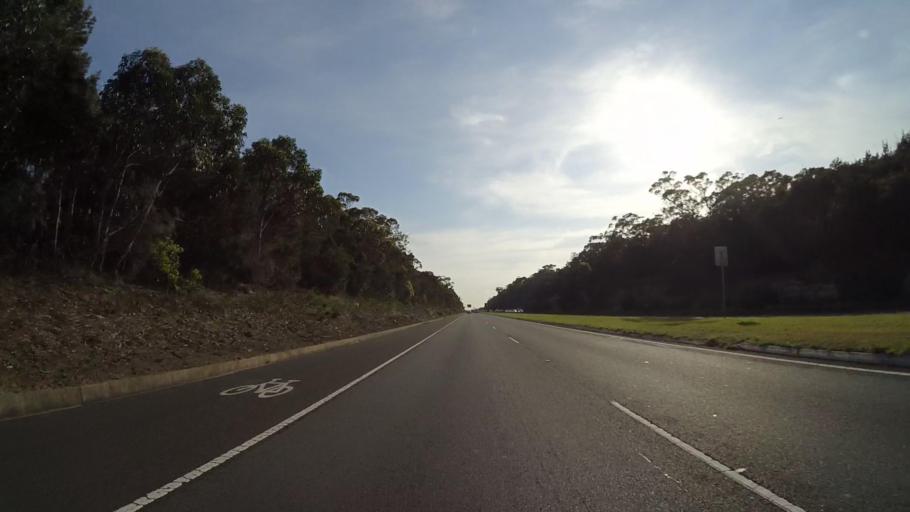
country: AU
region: New South Wales
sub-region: Sutherland Shire
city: Loftus
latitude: -34.0560
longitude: 151.0418
